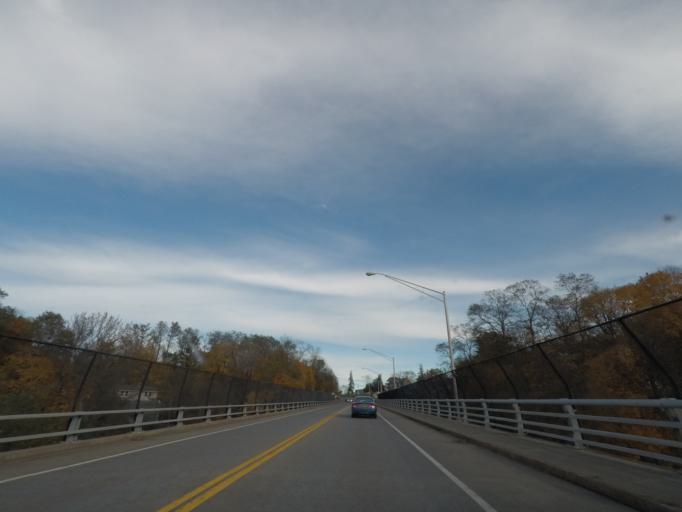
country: US
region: New York
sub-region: Albany County
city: Delmar
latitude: 42.6340
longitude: -73.7980
